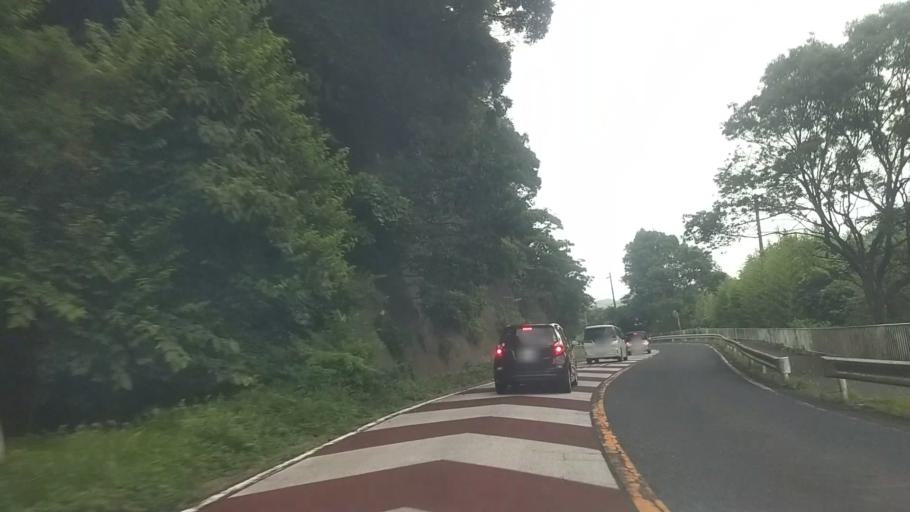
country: JP
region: Chiba
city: Ohara
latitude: 35.2663
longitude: 140.3700
